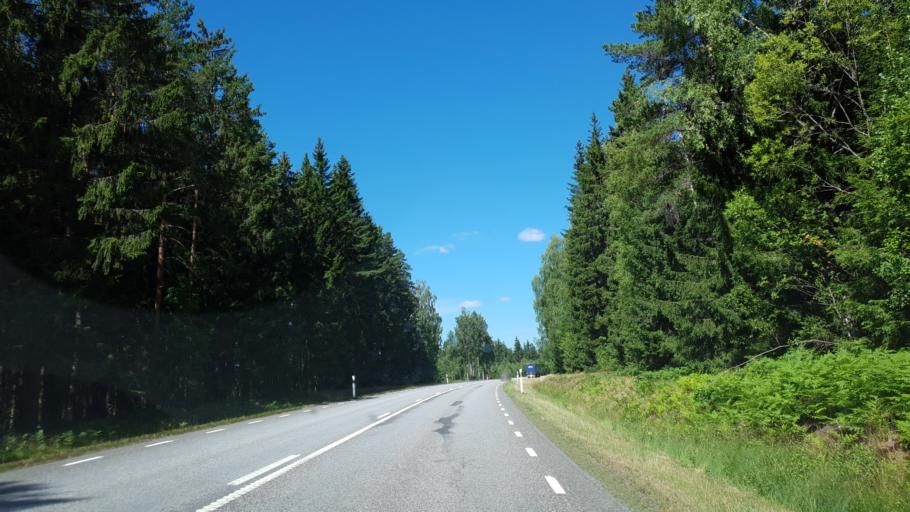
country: SE
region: Joenkoeping
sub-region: Varnamo Kommun
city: Rydaholm
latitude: 56.9751
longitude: 14.3139
